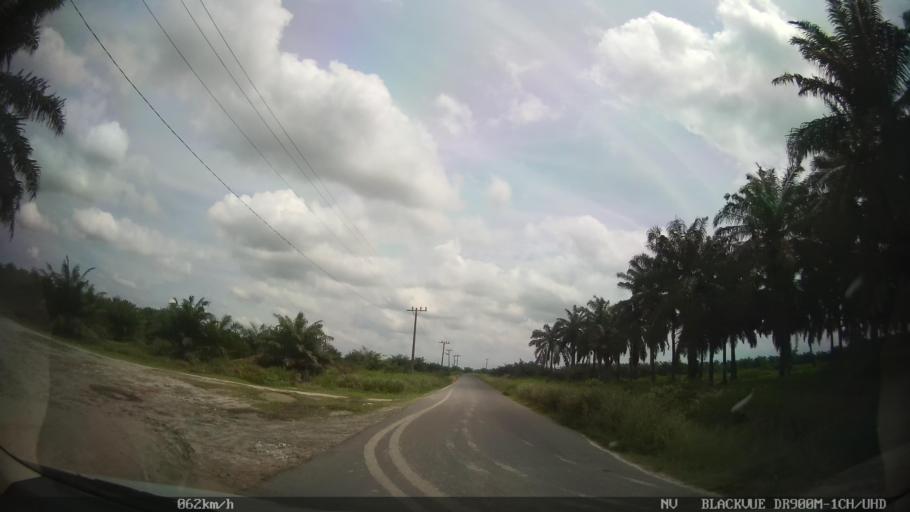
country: ID
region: North Sumatra
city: Percut
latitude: 3.5914
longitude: 98.8405
